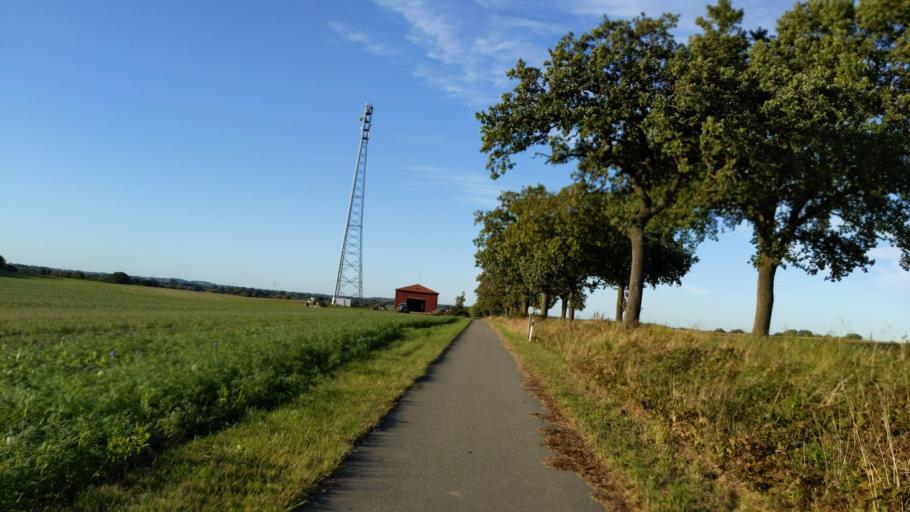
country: DE
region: Schleswig-Holstein
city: Ahrensbok
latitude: 54.0380
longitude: 10.5620
